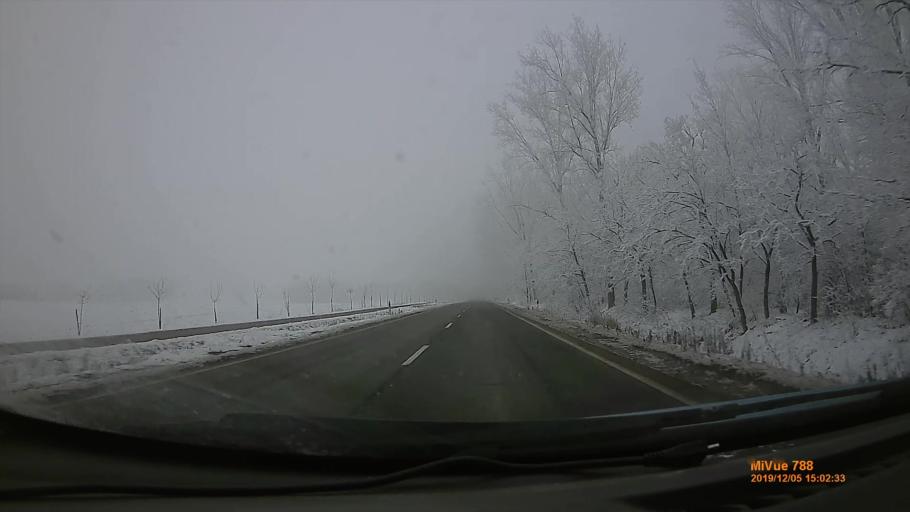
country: HU
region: Szabolcs-Szatmar-Bereg
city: Tiszanagyfalu
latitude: 48.0770
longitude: 21.5124
